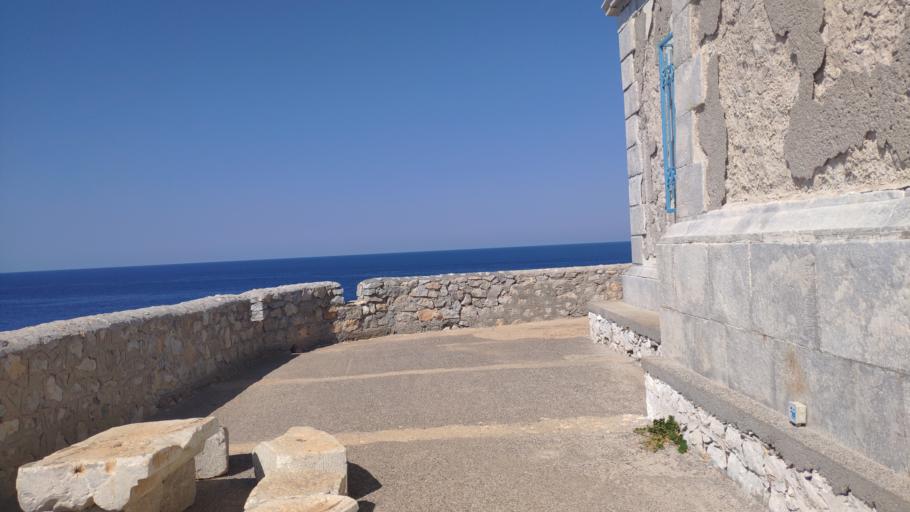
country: GR
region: Peloponnese
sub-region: Nomos Lakonias
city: Gytheio
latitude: 36.3860
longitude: 22.4830
